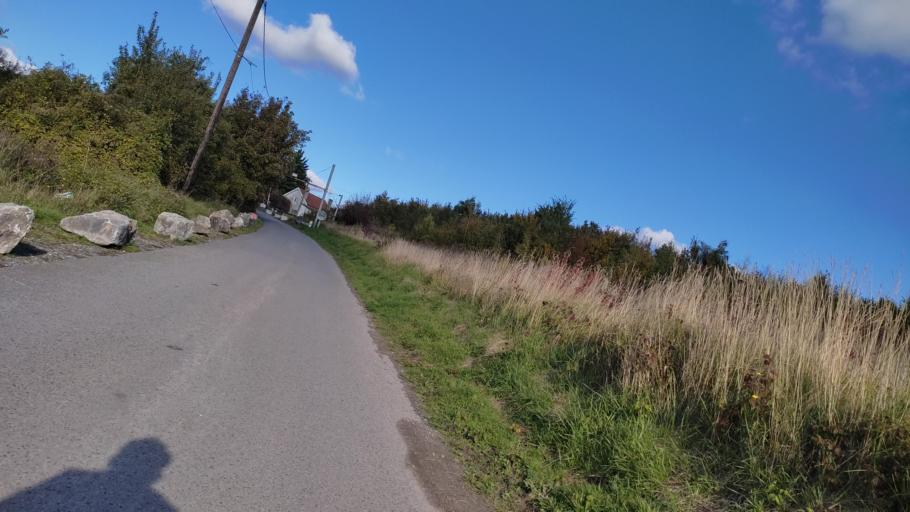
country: FR
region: Nord-Pas-de-Calais
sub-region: Departement du Pas-de-Calais
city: Saint-Laurent-Blangy
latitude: 50.3096
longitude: 2.8218
